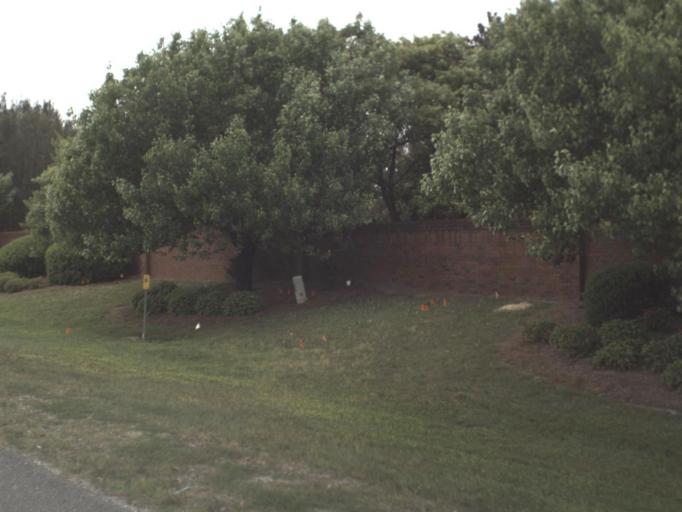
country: US
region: Florida
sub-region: Santa Rosa County
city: Oriole Beach
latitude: 30.3755
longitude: -87.1171
